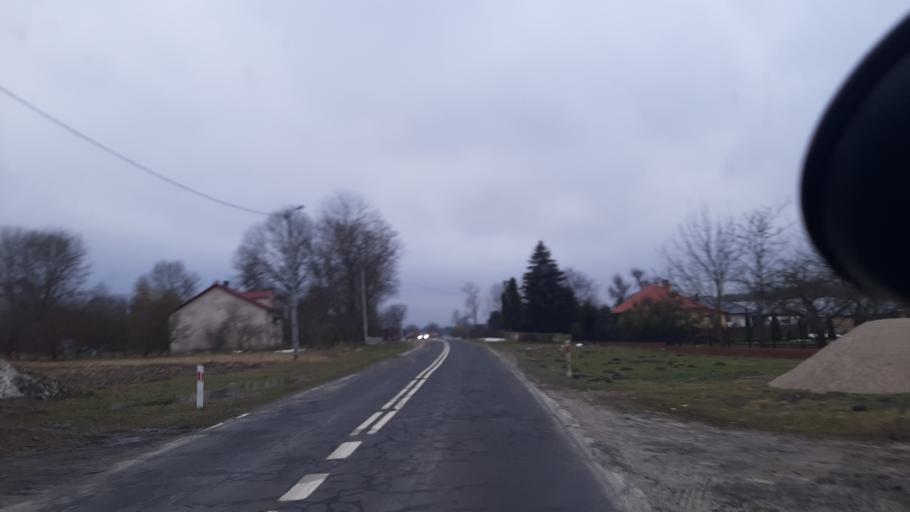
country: PL
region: Lublin Voivodeship
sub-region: Powiat parczewski
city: Podedworze
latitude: 51.5600
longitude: 23.2835
